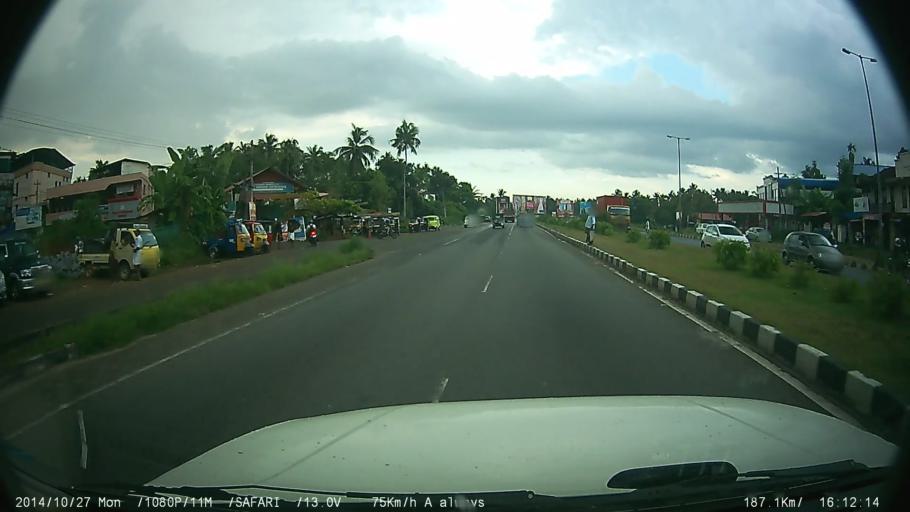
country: IN
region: Kerala
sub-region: Thrissur District
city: Irinjalakuda
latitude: 10.4047
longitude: 76.2775
